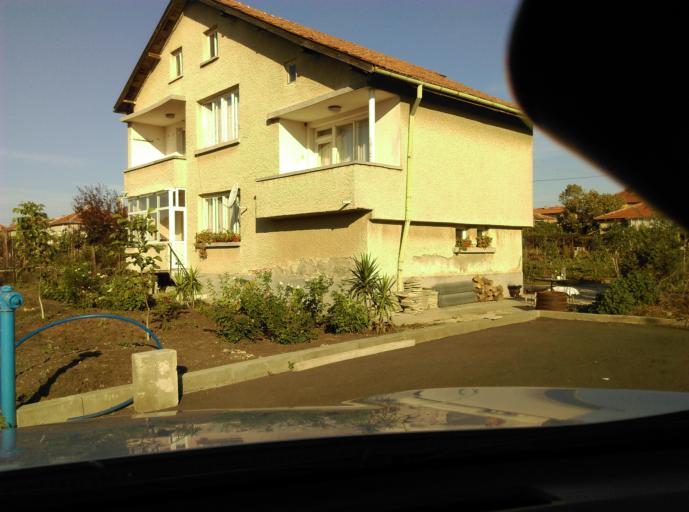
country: BG
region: Burgas
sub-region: Obshtina Kameno
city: Kameno
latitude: 42.6000
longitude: 27.3874
